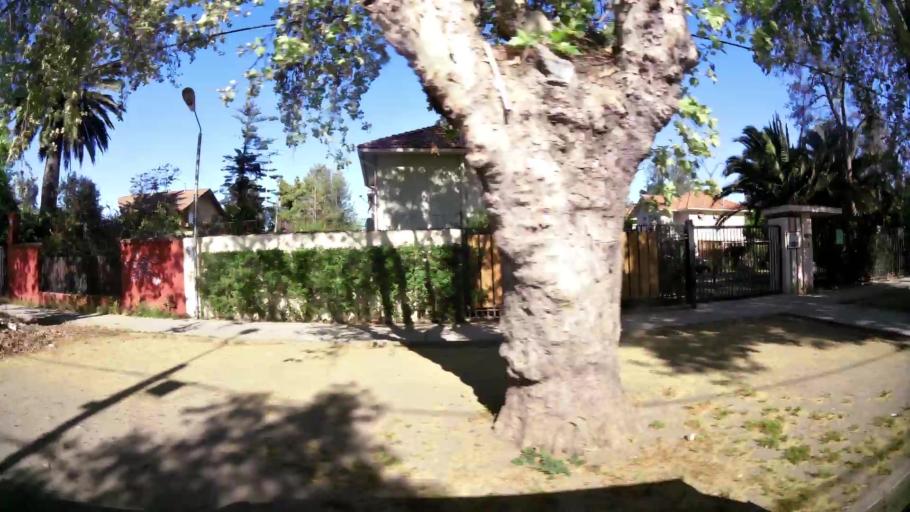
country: CL
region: Santiago Metropolitan
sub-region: Provincia de Talagante
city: Penaflor
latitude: -33.6014
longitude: -70.8682
